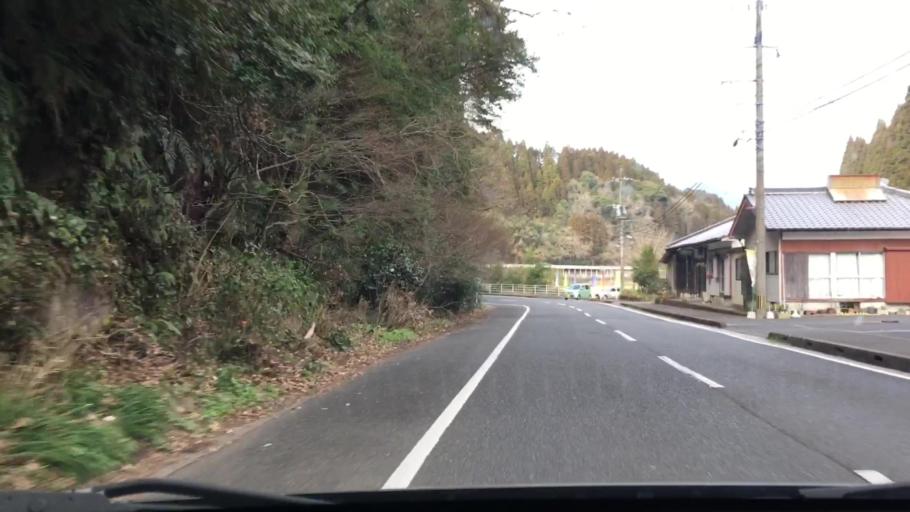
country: JP
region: Miyazaki
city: Kushima
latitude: 31.5448
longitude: 131.2423
